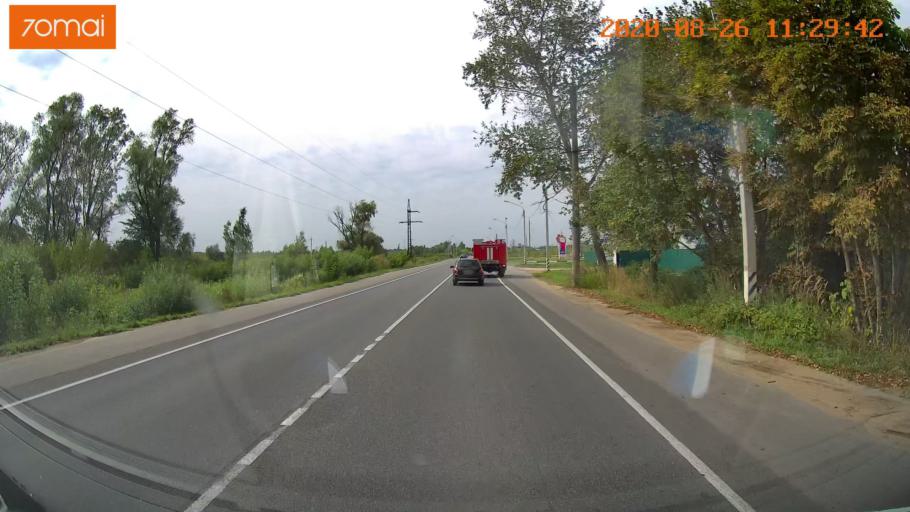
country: RU
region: Rjazan
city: Shilovo
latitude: 54.3185
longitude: 40.8954
